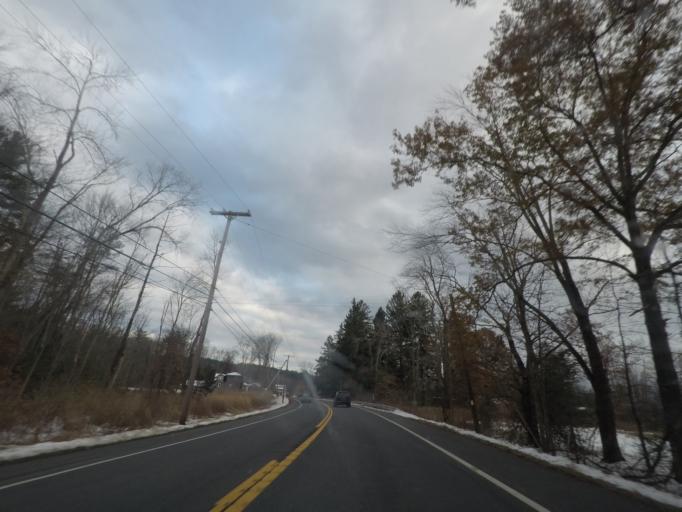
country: US
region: New York
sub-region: Ulster County
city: Tillson
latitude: 41.8209
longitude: -74.0619
